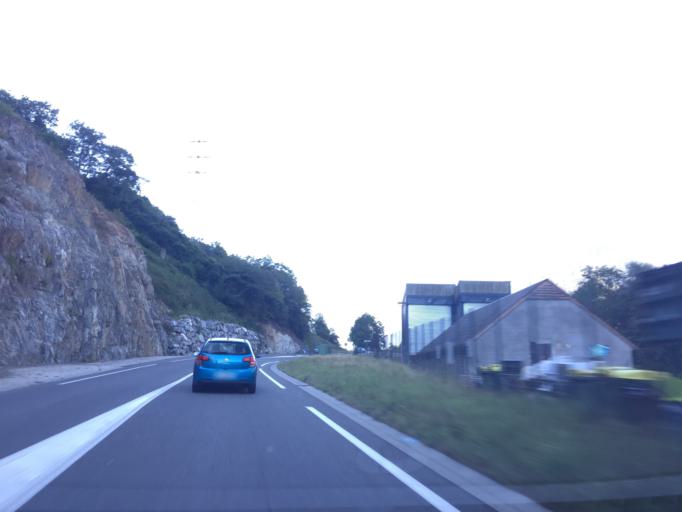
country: FR
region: Midi-Pyrenees
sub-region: Departement des Hautes-Pyrenees
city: Saint-Lary-Soulan
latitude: 42.8822
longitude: 0.3497
